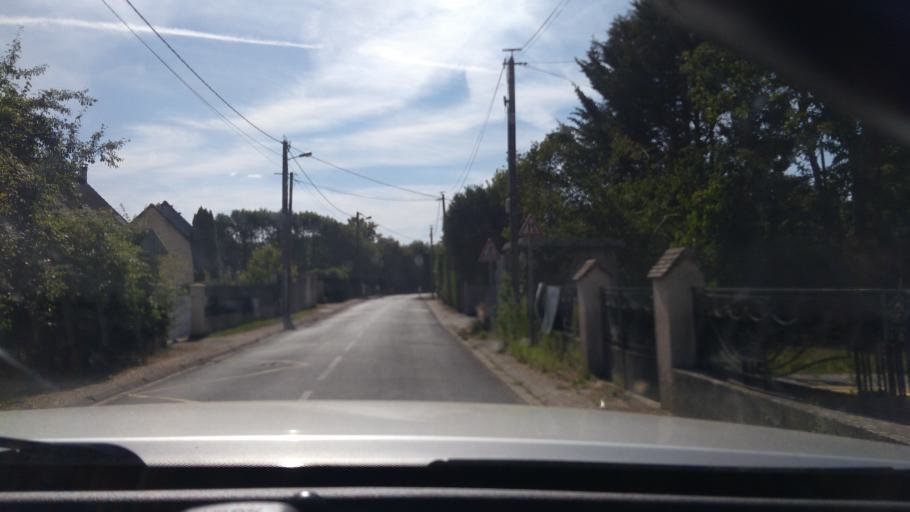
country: FR
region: Ile-de-France
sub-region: Departement de Seine-et-Marne
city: Chartrettes
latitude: 48.4852
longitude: 2.7085
